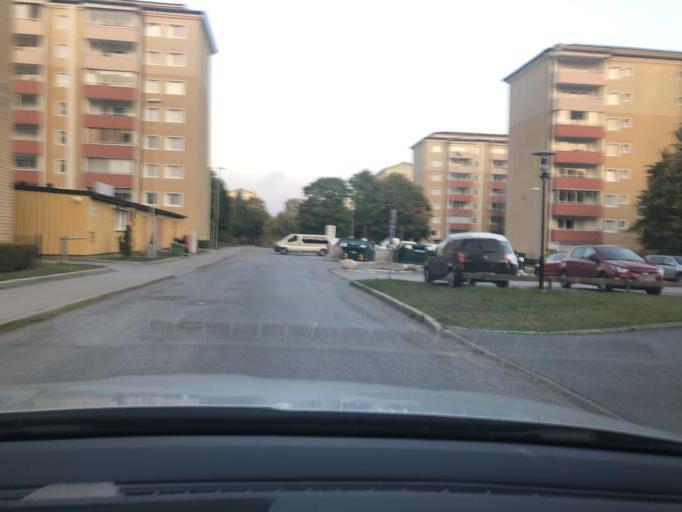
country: SE
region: Stockholm
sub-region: Botkyrka Kommun
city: Eriksberg
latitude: 59.2464
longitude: 17.8240
